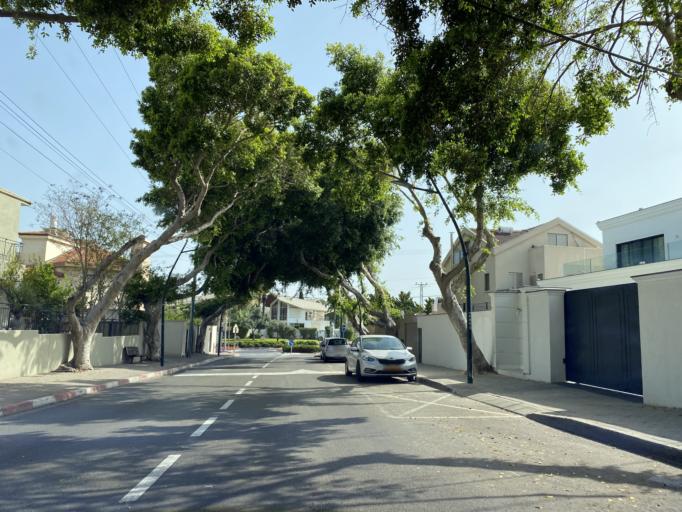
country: IL
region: Tel Aviv
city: Herzliya Pituah
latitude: 32.1686
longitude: 34.8061
